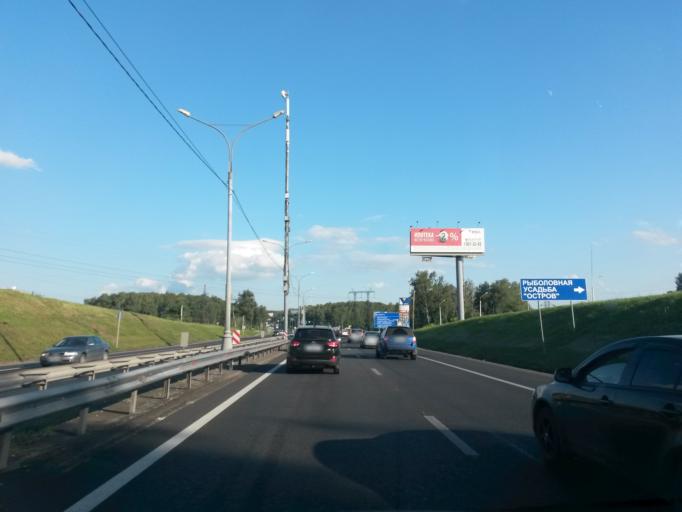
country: RU
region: Moskovskaya
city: Petrovskaya
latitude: 55.5598
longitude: 37.7756
